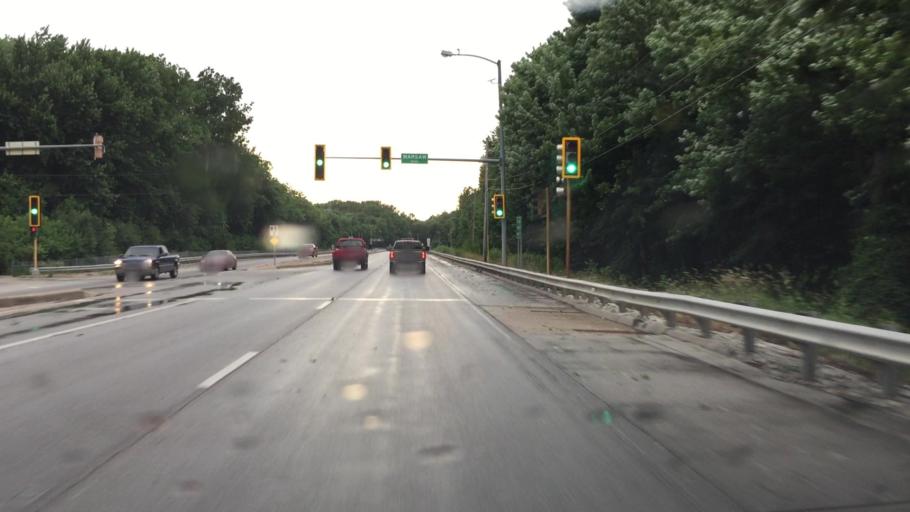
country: US
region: Illinois
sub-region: Hancock County
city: Hamilton
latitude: 40.3903
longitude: -91.3591
